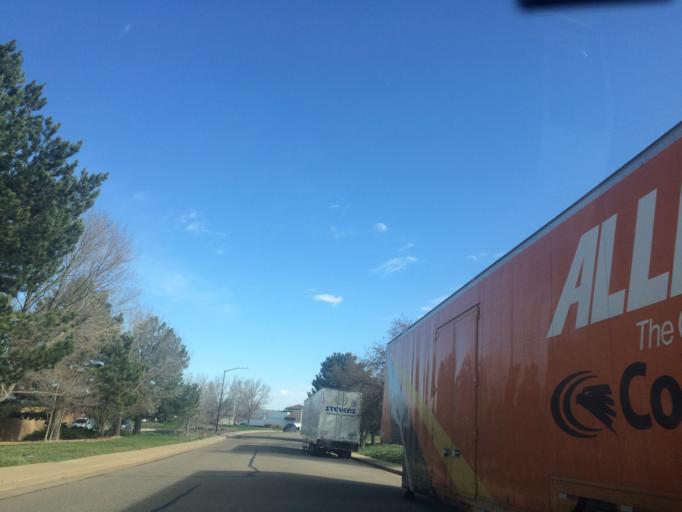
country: US
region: Colorado
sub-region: Boulder County
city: Lafayette
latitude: 40.0022
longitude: -105.1060
